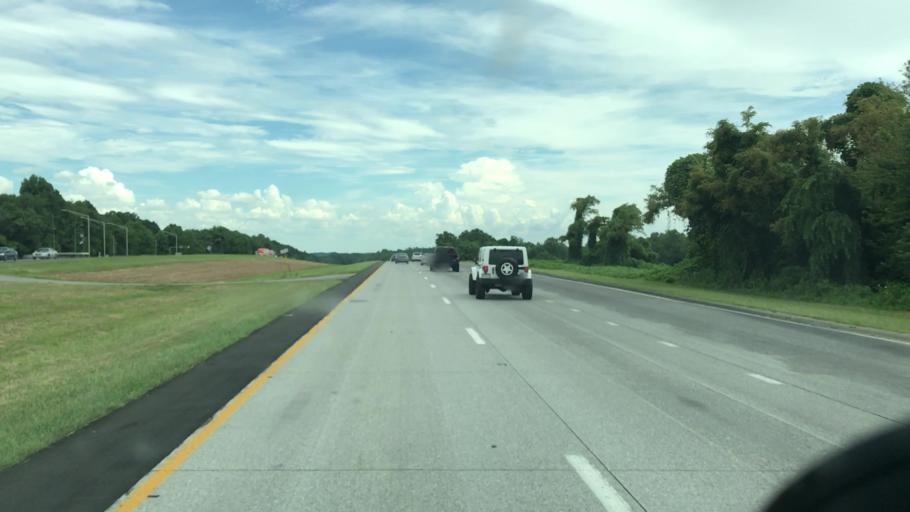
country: US
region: Virginia
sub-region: Carroll County
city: Cana
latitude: 36.5319
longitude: -80.7501
